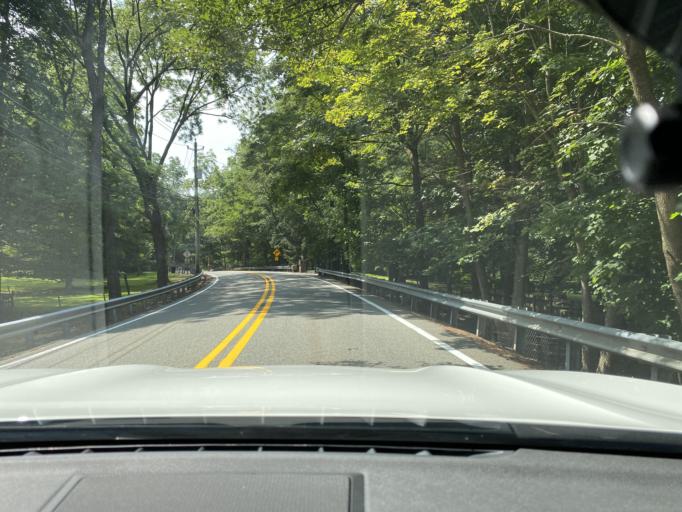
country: US
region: New Jersey
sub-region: Bergen County
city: Franklin Lakes
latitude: 41.0644
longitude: -74.2087
